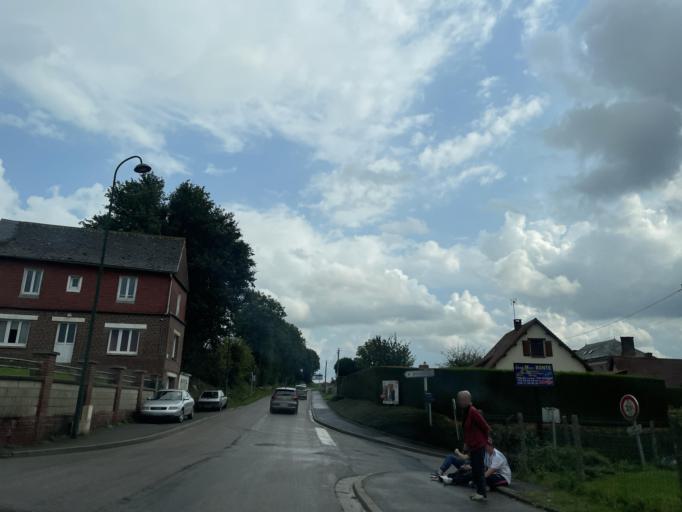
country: FR
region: Haute-Normandie
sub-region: Departement de la Seine-Maritime
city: Envermeu
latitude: 49.8894
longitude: 1.2798
